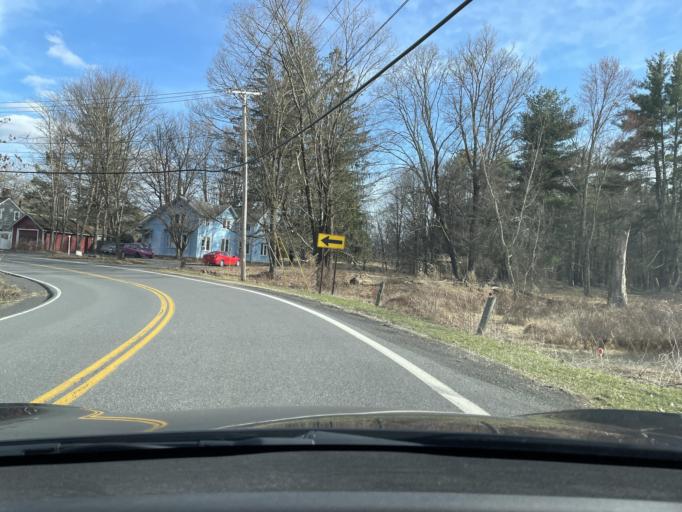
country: US
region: New York
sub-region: Ulster County
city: Zena
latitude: 42.0344
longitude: -74.0856
